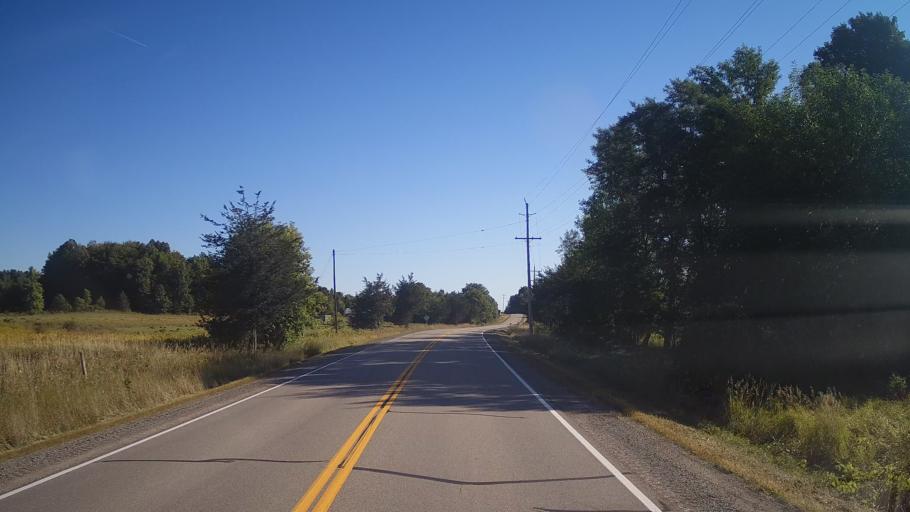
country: CA
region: Ontario
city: Gananoque
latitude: 44.5876
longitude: -76.1050
